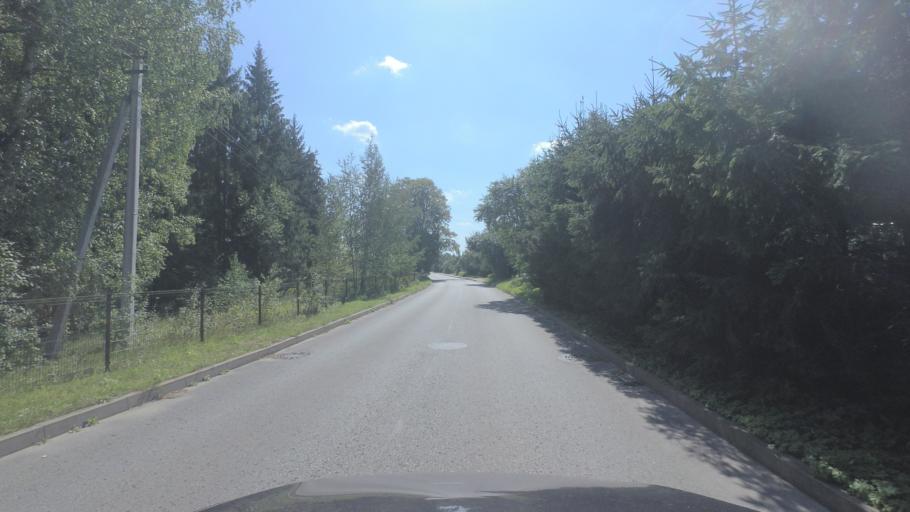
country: LT
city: Nemencine
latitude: 54.8424
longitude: 25.3713
